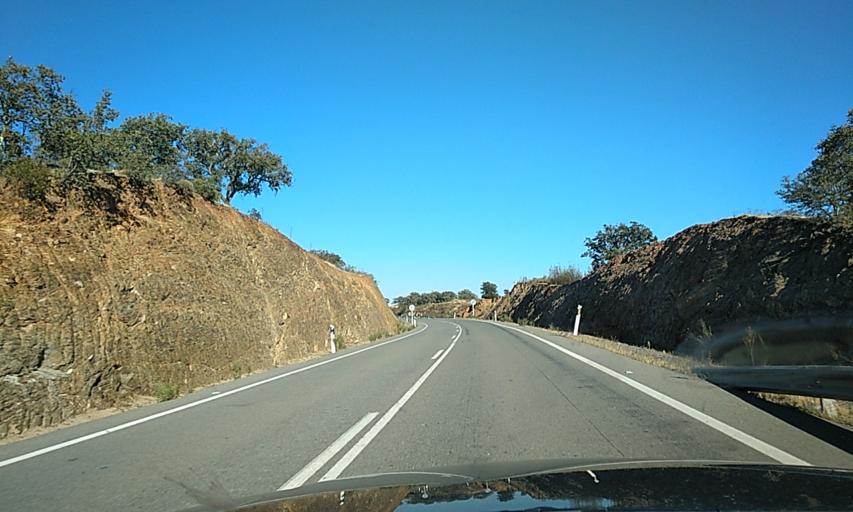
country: ES
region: Andalusia
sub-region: Provincia de Huelva
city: Santa Barbara de Casa
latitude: 37.7898
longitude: -7.1768
